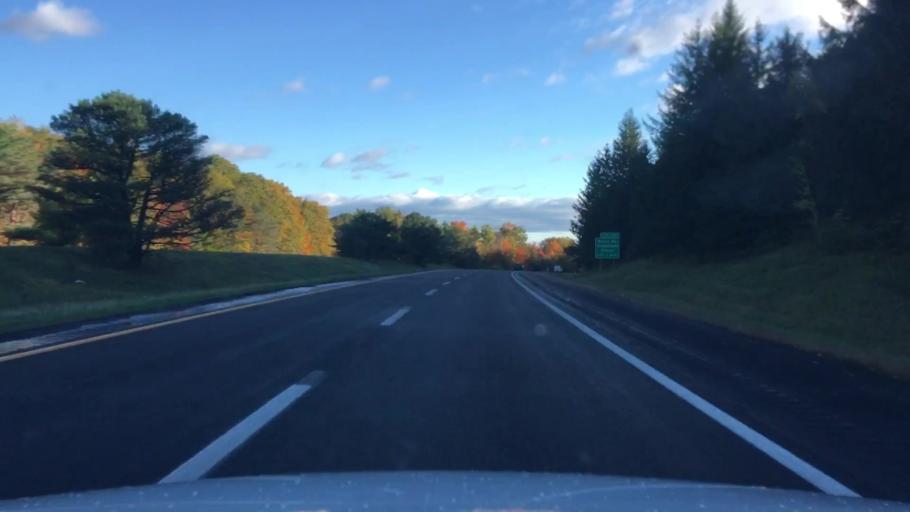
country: US
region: Maine
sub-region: Penobscot County
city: Veazie
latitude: 44.8568
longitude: -68.7214
